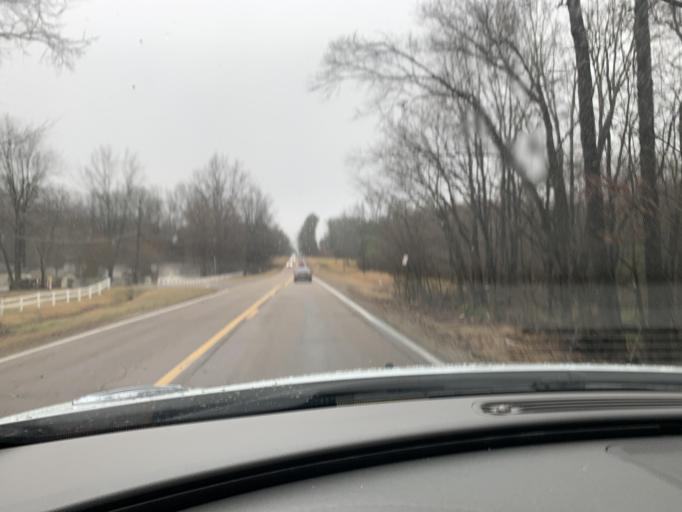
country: US
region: Mississippi
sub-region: De Soto County
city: Hernando
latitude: 34.8768
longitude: -89.9957
